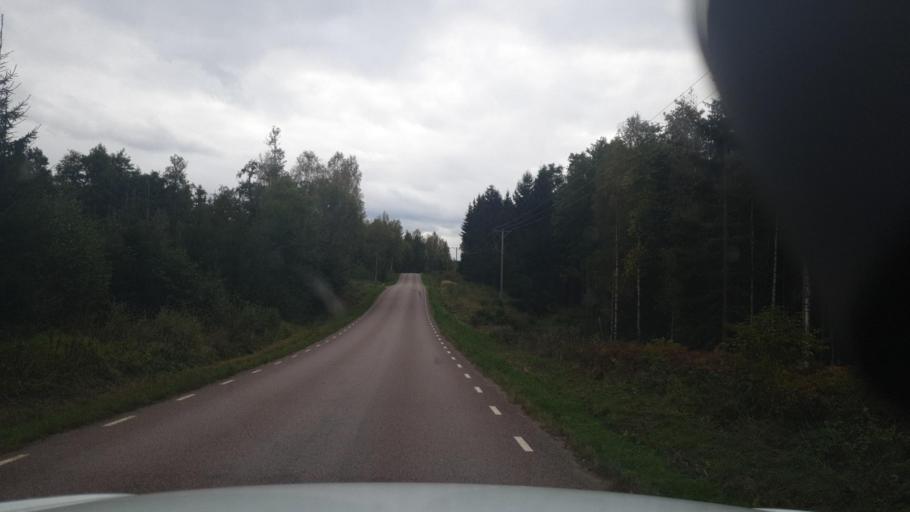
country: SE
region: Vaermland
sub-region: Karlstads Kommun
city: Valberg
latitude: 59.4459
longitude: 13.0910
